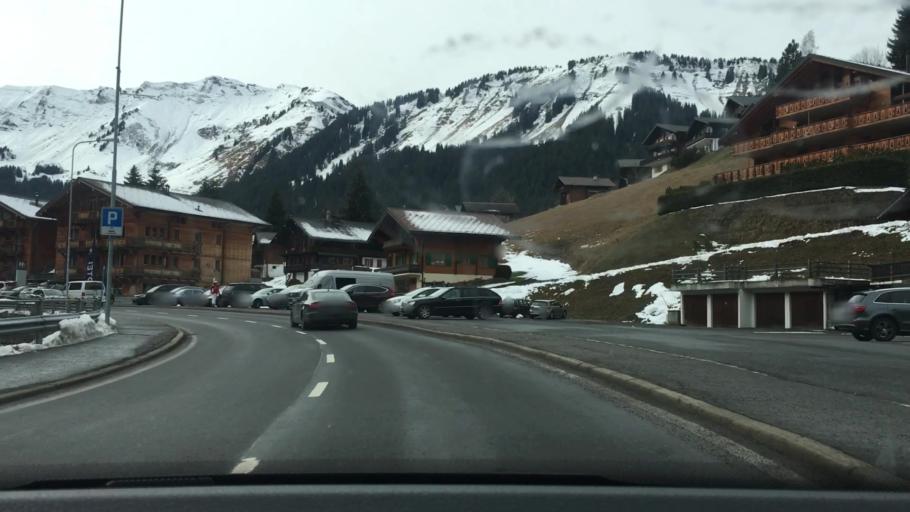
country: FR
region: Rhone-Alpes
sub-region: Departement de la Haute-Savoie
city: Chatel
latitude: 46.2385
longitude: 6.8619
